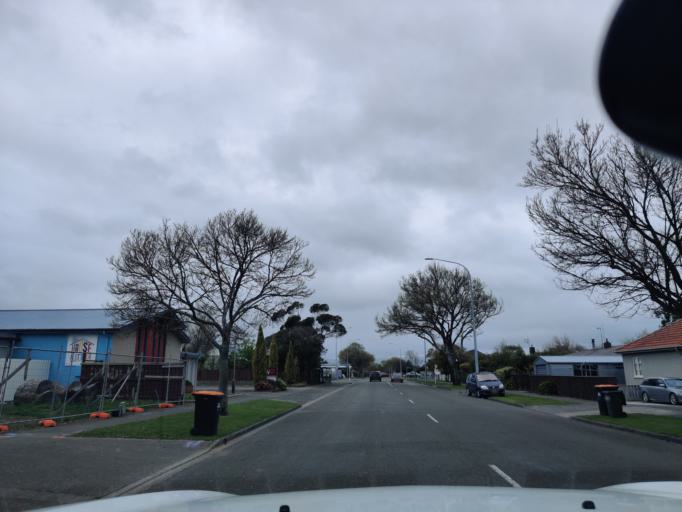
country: NZ
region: Manawatu-Wanganui
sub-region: Palmerston North City
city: Palmerston North
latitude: -40.3357
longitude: 175.6342
